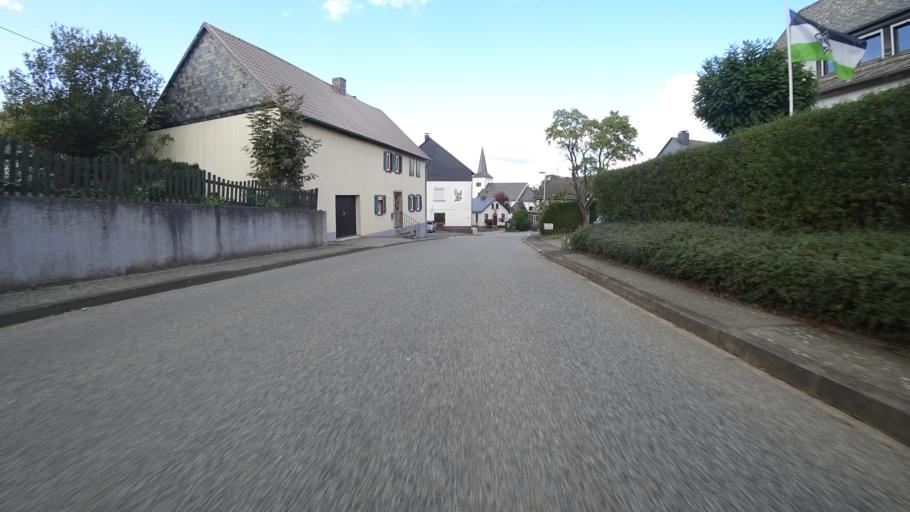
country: DE
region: Rheinland-Pfalz
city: Liebshausen
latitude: 50.0320
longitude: 7.6307
